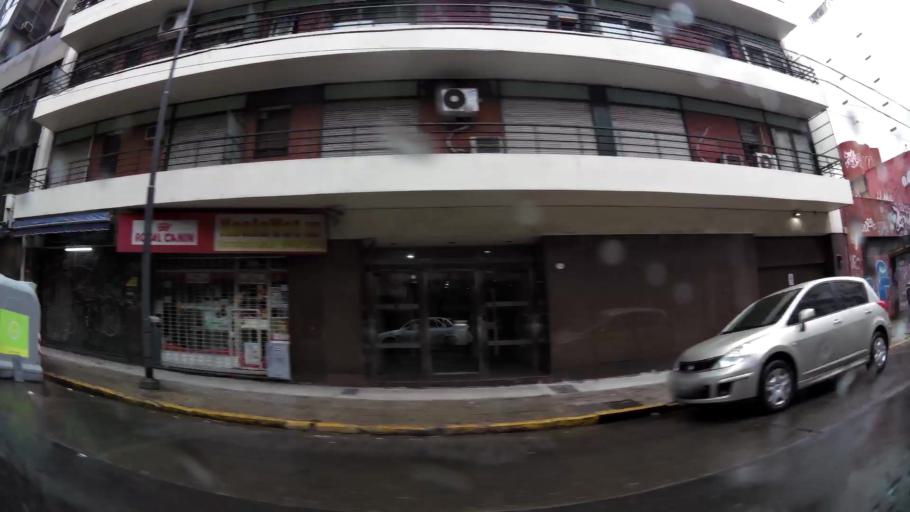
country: AR
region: Buenos Aires F.D.
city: Retiro
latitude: -34.5980
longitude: -58.4013
